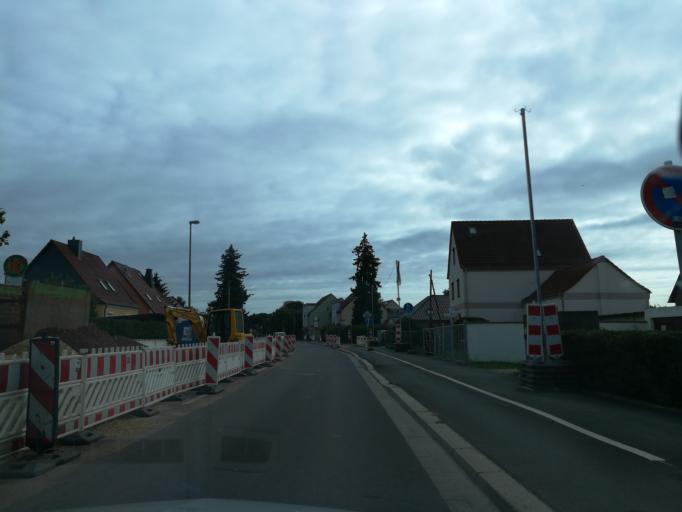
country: DE
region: Saxony-Anhalt
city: Neue Neustadt
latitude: 52.1485
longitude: 11.6081
